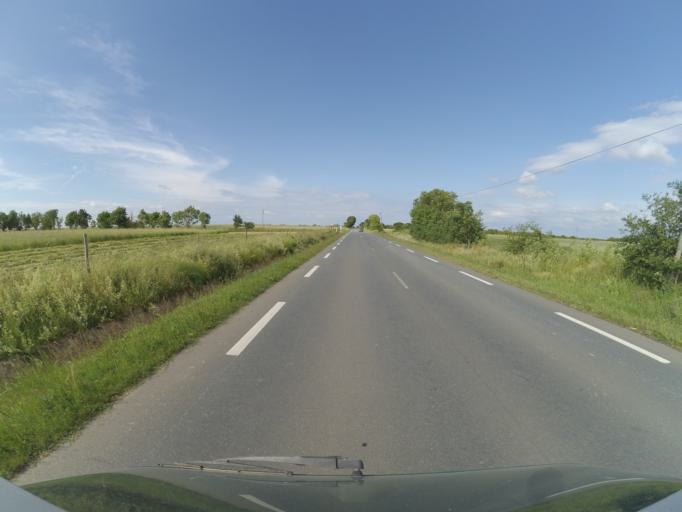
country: FR
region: Poitou-Charentes
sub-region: Departement de la Charente-Maritime
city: Saint-Xandre
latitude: 46.2294
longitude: -1.0785
